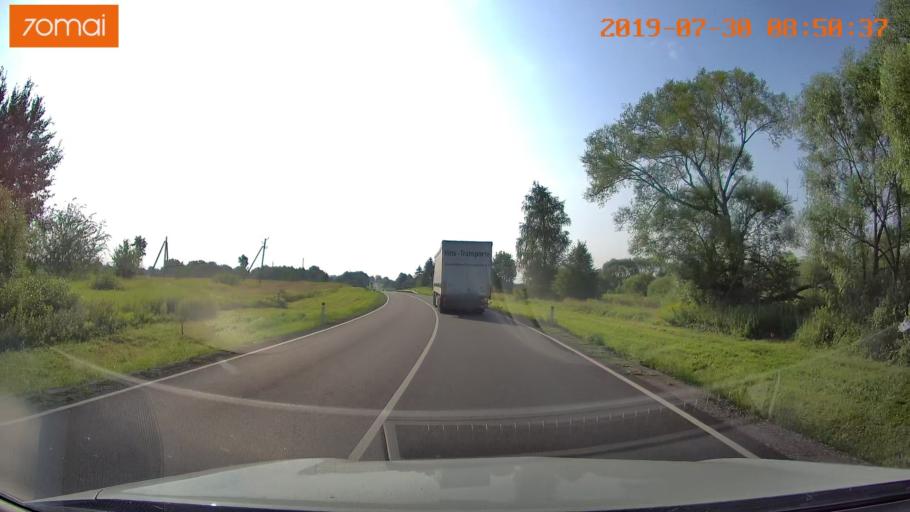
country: RU
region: Kaliningrad
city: Chernyakhovsk
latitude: 54.6062
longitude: 21.9424
